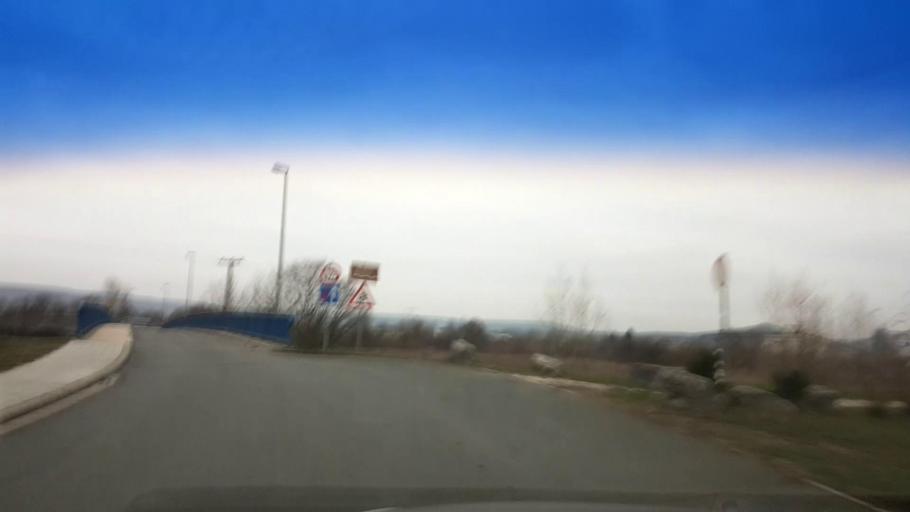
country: DE
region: Bavaria
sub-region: Upper Franconia
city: Altendorf
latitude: 49.7914
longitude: 11.0035
